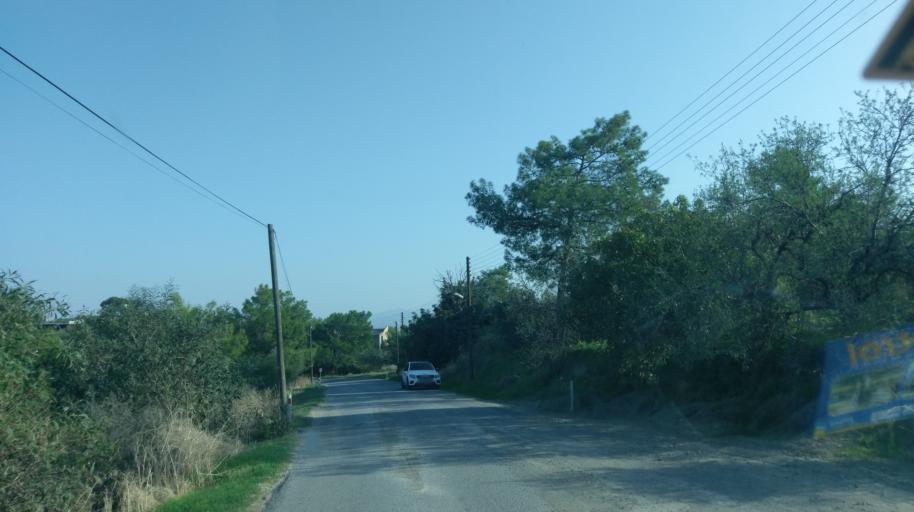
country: CY
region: Lefkosia
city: Kato Pyrgos
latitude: 35.1585
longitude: 32.7638
